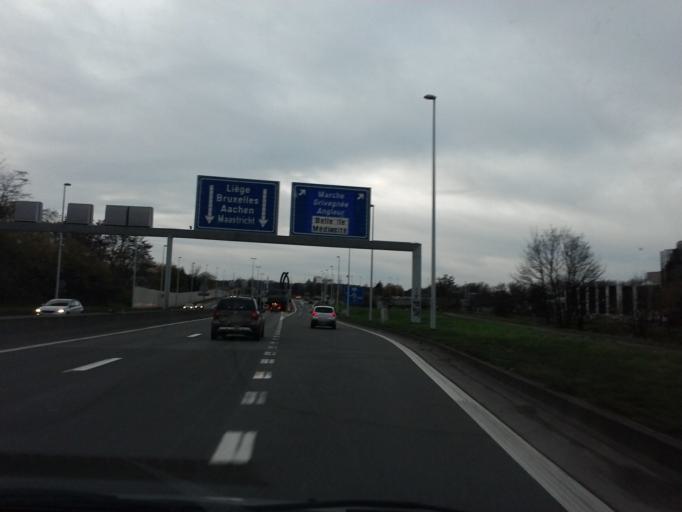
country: BE
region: Wallonia
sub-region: Province de Liege
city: Chaudfontaine
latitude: 50.6124
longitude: 5.6061
